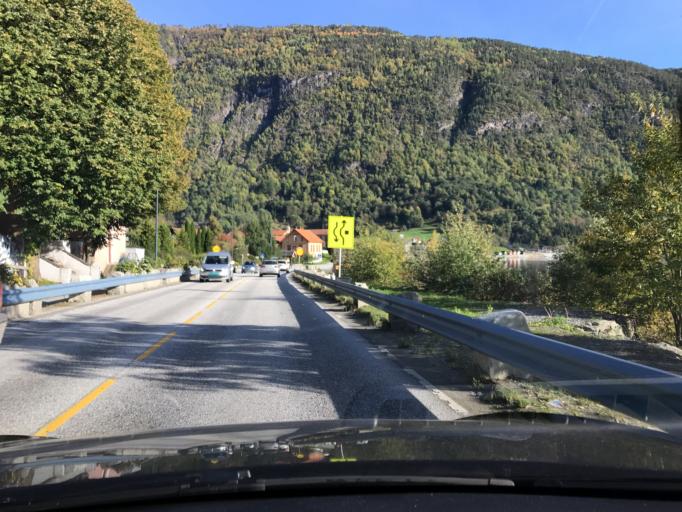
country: NO
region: Sogn og Fjordane
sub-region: Sogndal
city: Sogndalsfjora
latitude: 61.2322
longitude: 7.1127
